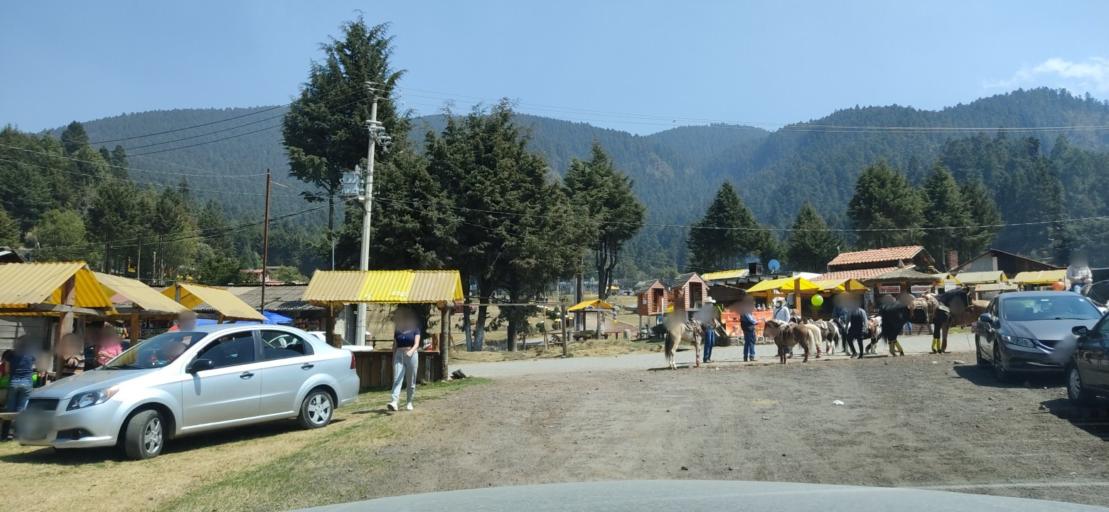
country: MX
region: Mexico
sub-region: Ocoyoacac
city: San Jeronimo Acazulco
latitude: 19.2450
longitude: -99.3775
